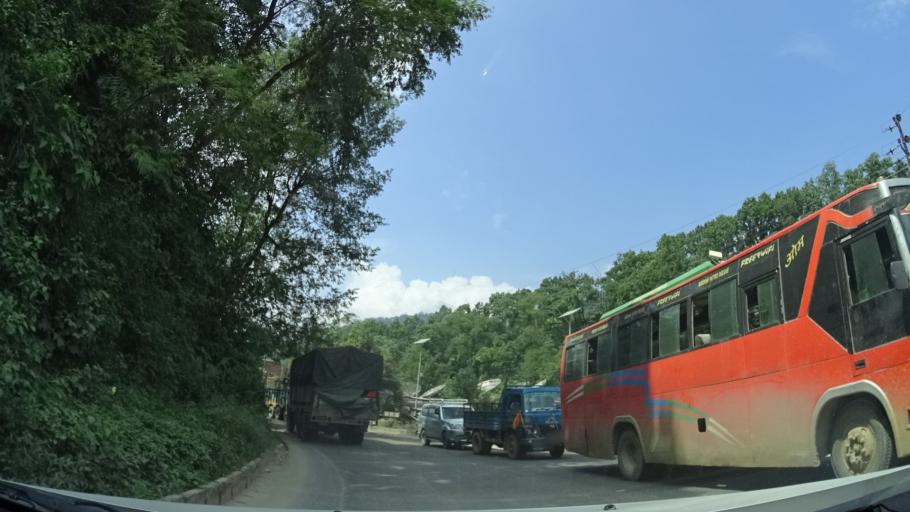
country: NP
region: Central Region
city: Kirtipur
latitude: 27.8001
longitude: 84.9941
